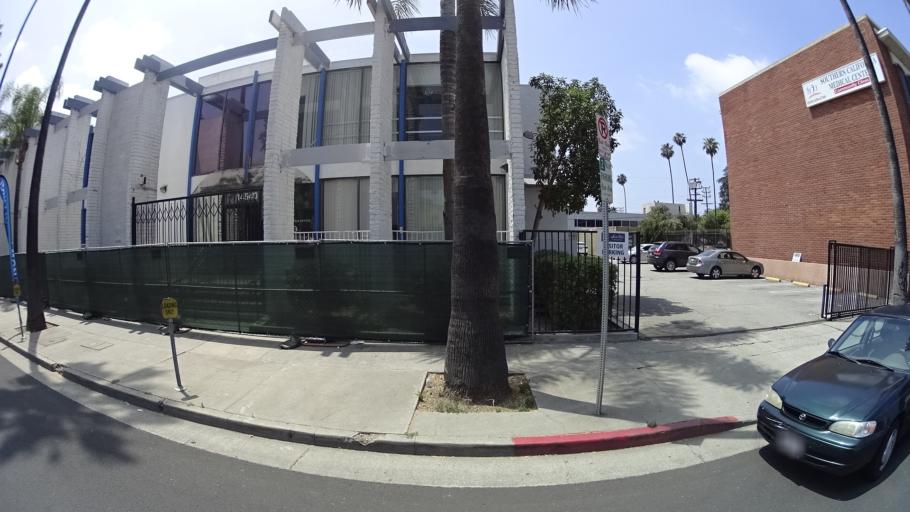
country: US
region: California
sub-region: Los Angeles County
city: Van Nuys
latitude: 34.1899
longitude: -118.4504
